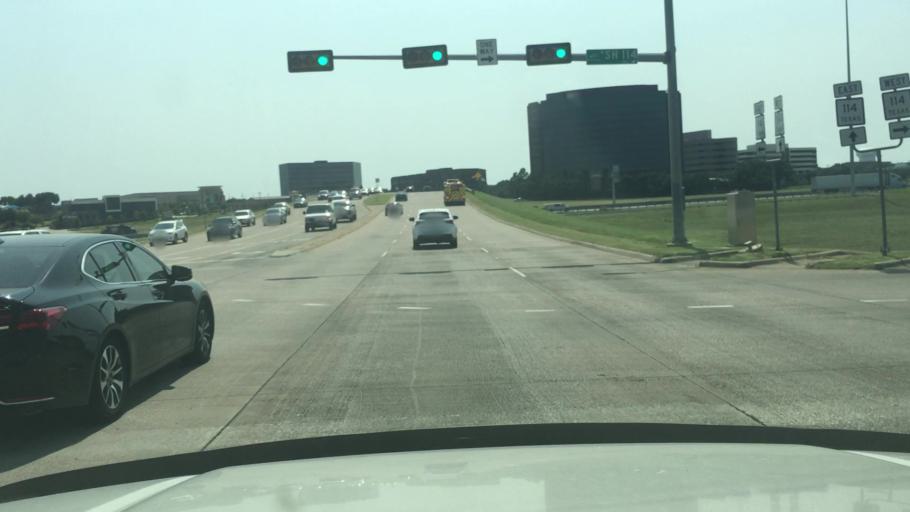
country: US
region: Texas
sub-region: Dallas County
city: Farmers Branch
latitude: 32.8921
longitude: -96.9614
